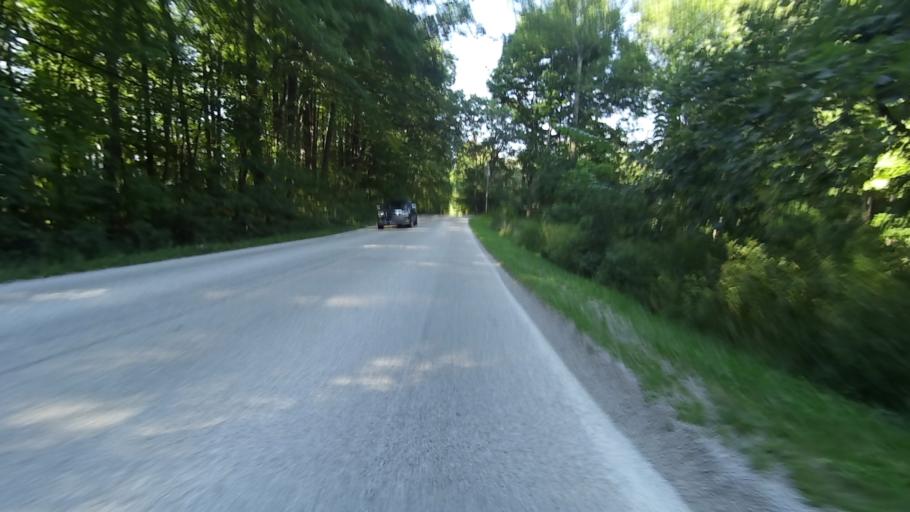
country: US
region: Ohio
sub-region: Portage County
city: Streetsboro
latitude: 41.2524
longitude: -81.2855
